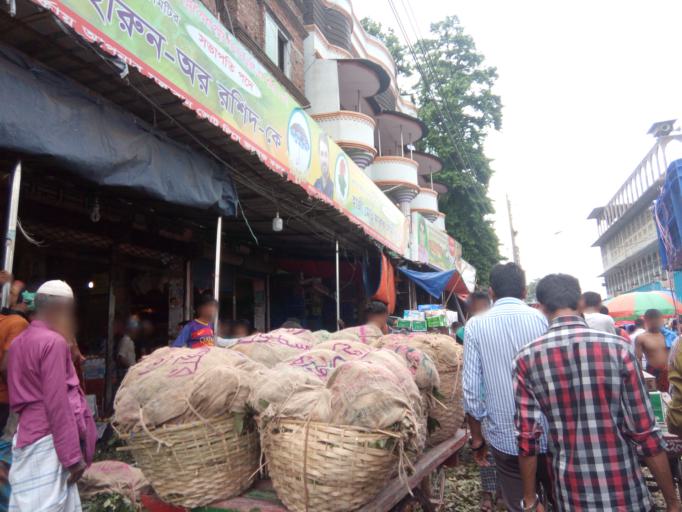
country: BD
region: Dhaka
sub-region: Dhaka
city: Dhaka
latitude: 23.7084
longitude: 90.4048
